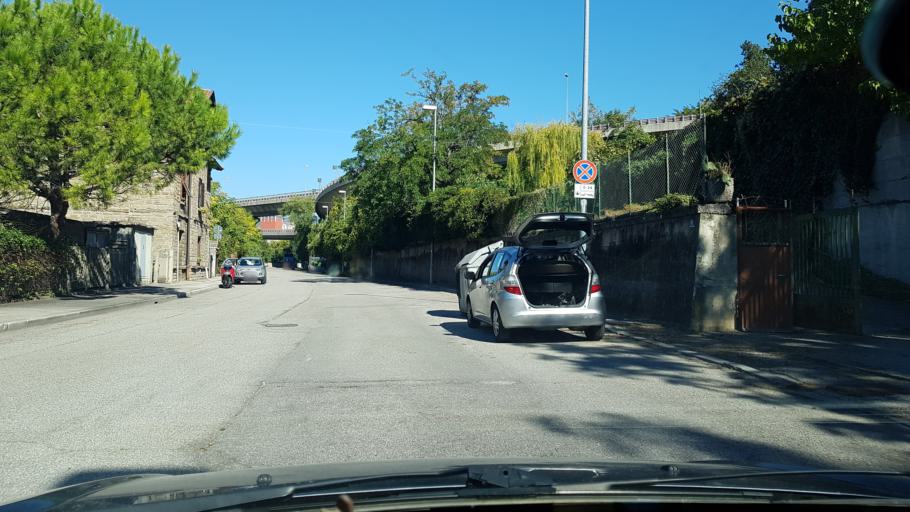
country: IT
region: Friuli Venezia Giulia
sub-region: Provincia di Trieste
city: Muggia
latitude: 45.6162
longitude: 13.7860
